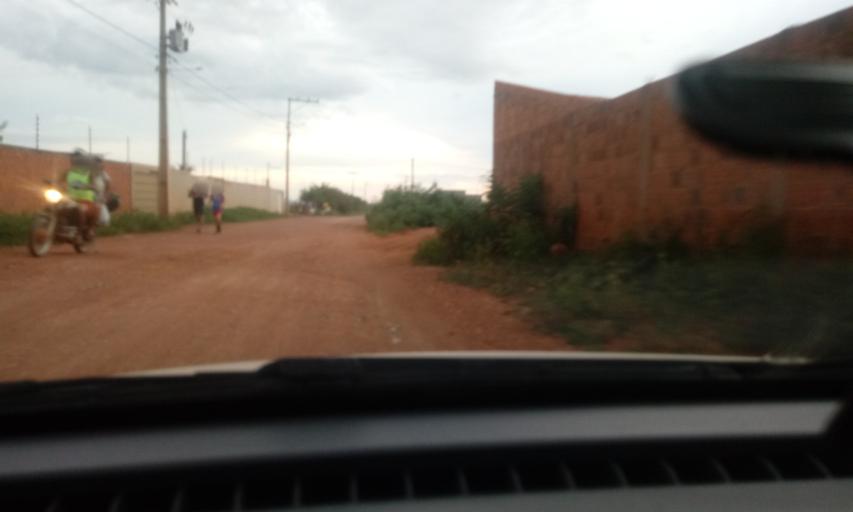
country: BR
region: Bahia
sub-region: Riacho De Santana
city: Riacho de Santana
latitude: -13.7834
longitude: -42.7239
